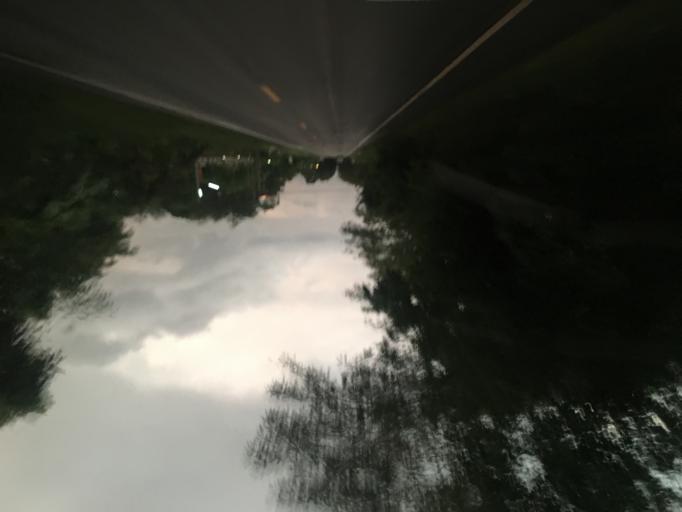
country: TH
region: Changwat Udon Thani
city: Udon Thani
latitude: 17.3300
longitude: 102.7141
